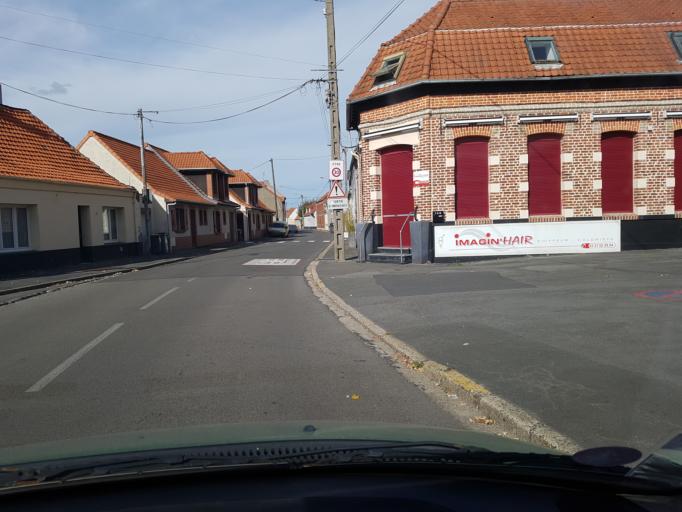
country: FR
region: Nord-Pas-de-Calais
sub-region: Departement du Pas-de-Calais
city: Labeuvriere
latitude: 50.5226
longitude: 2.5650
